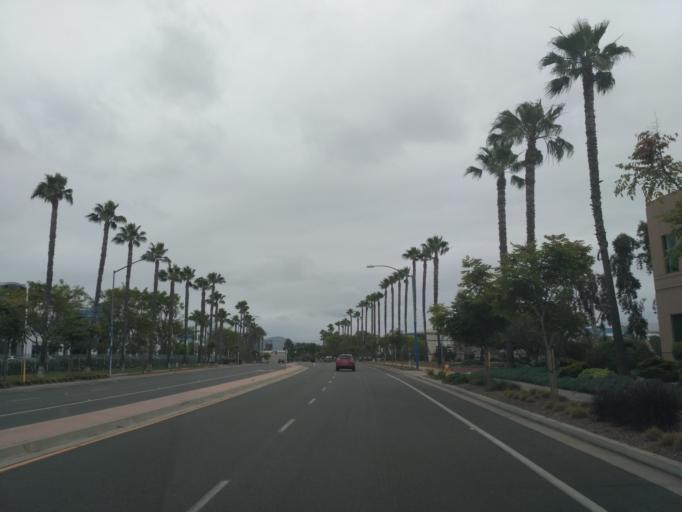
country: US
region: California
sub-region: San Diego County
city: San Diego
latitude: 32.8261
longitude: -117.1315
